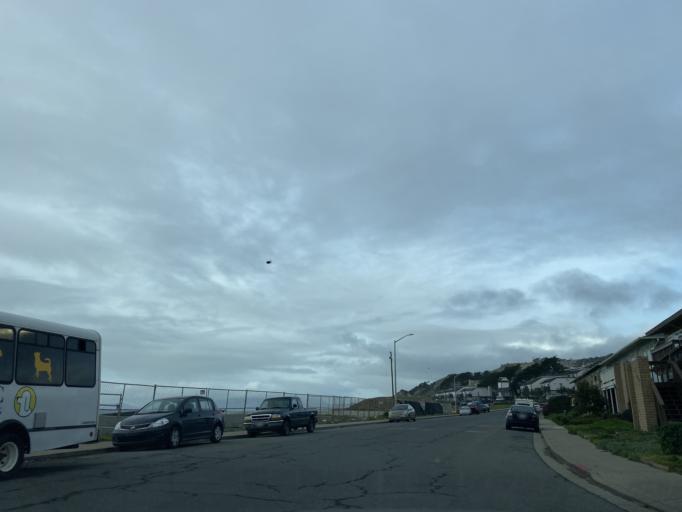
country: US
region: California
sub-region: San Mateo County
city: Broadmoor
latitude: 37.6530
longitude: -122.4929
